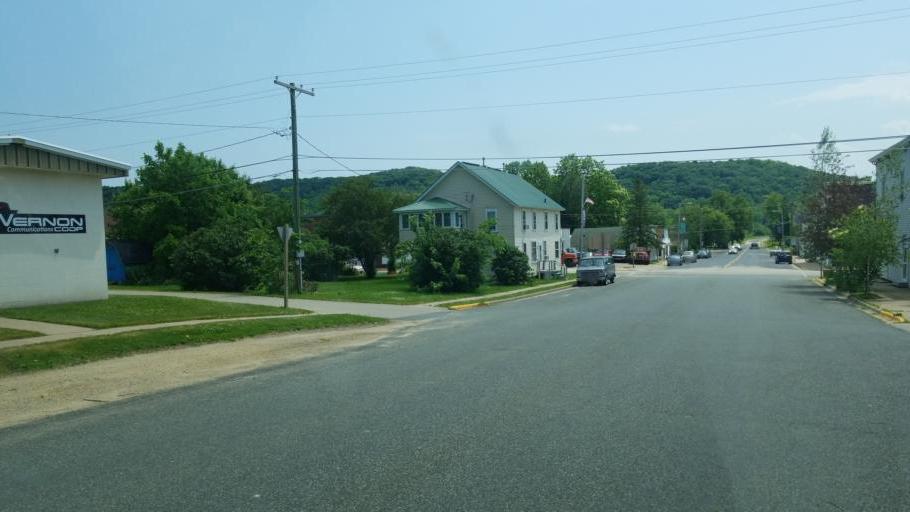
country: US
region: Wisconsin
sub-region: Monroe County
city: Cashton
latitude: 43.5750
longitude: -90.6364
